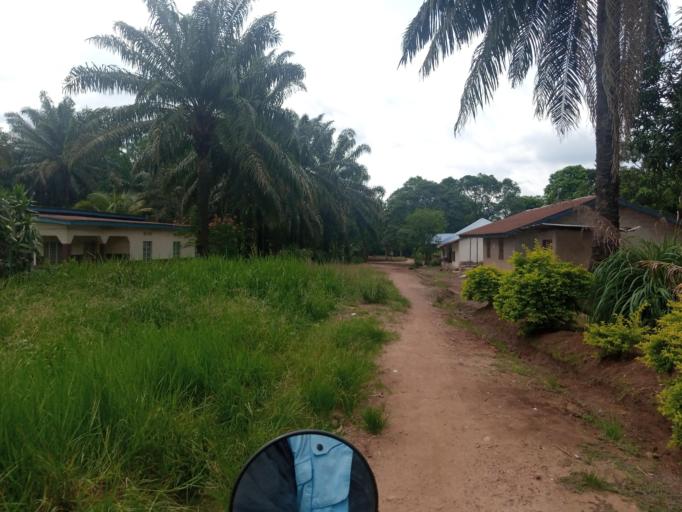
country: SL
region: Southern Province
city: Baoma
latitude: 7.9833
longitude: -11.7296
